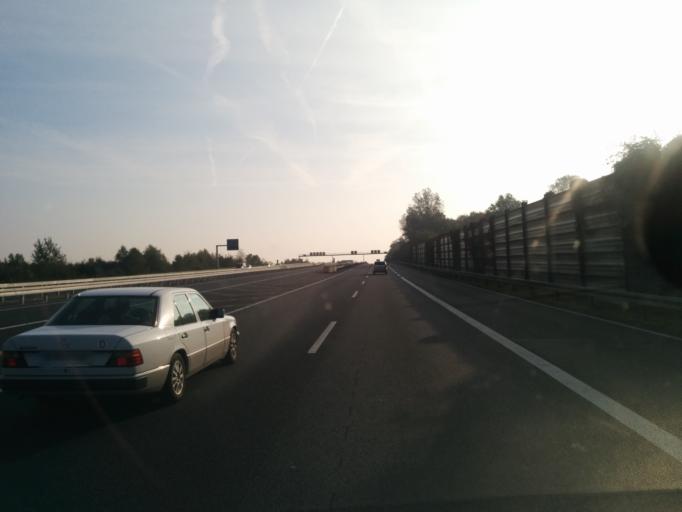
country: DE
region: Lower Saxony
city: Lehrte
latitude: 52.3898
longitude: 9.9666
